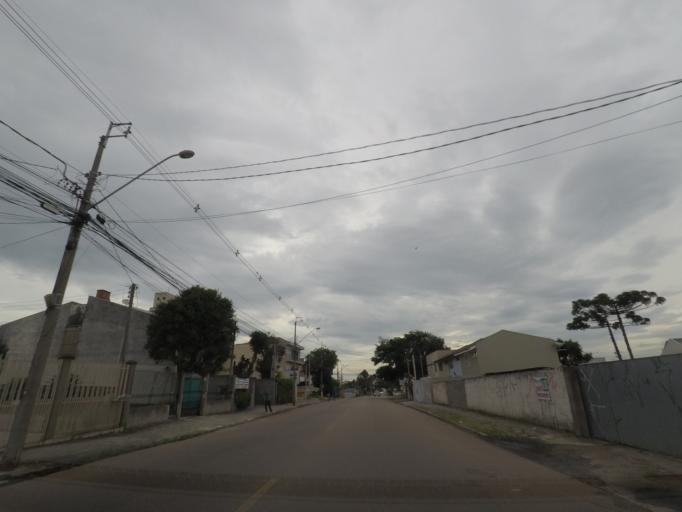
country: BR
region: Parana
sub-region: Curitiba
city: Curitiba
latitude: -25.4719
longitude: -49.3011
